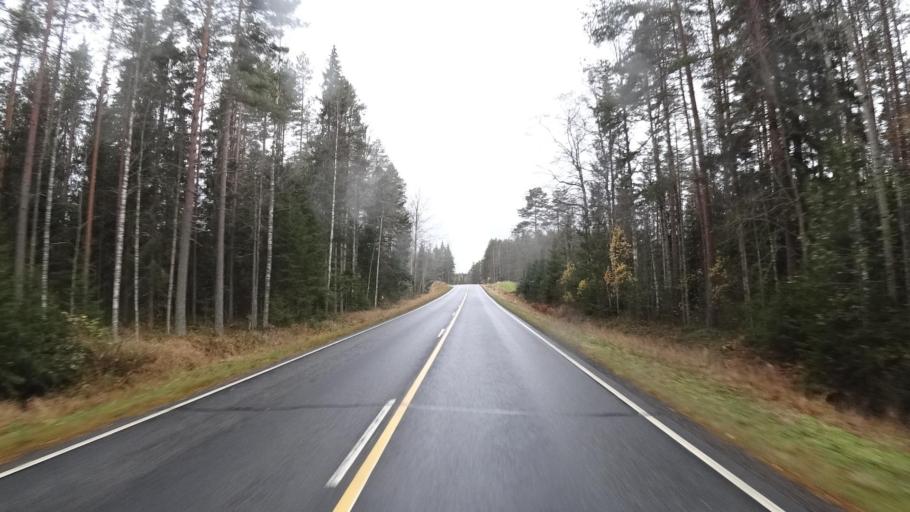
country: FI
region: Southern Savonia
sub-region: Mikkeli
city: Kangasniemi
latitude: 62.1618
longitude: 26.8345
